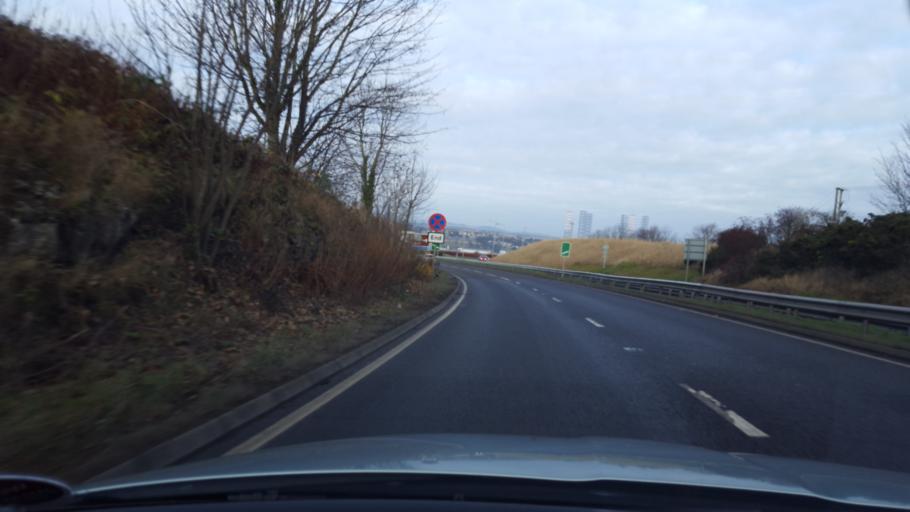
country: GB
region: Scotland
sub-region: Fife
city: Newport-On-Tay
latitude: 56.4451
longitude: -2.9314
